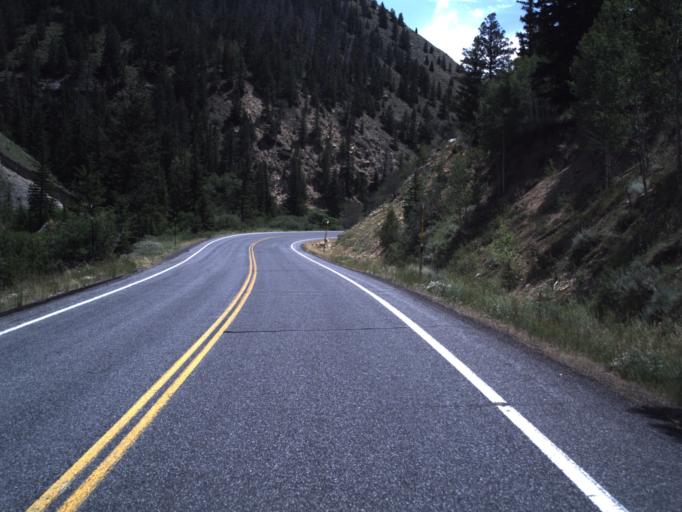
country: US
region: Utah
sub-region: Emery County
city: Huntington
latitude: 39.4829
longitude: -111.1586
